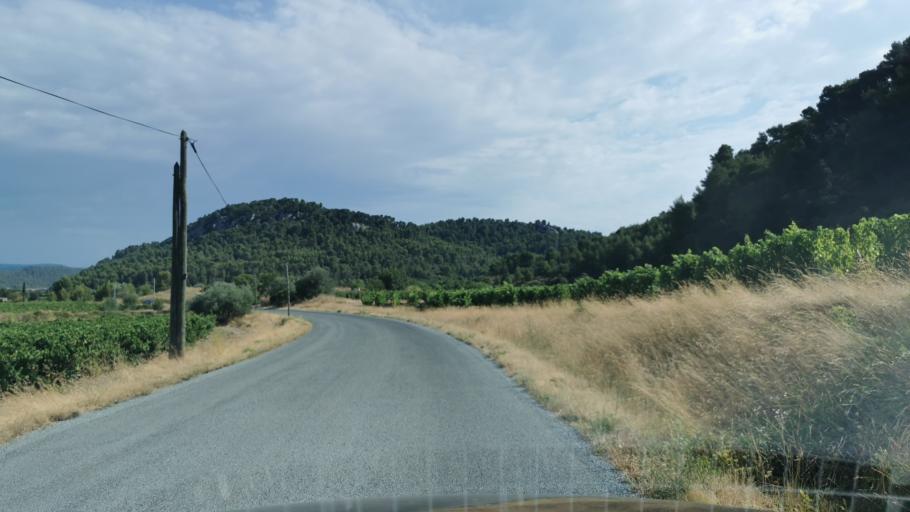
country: FR
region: Languedoc-Roussillon
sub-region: Departement de l'Aude
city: Bize-Minervois
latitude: 43.3213
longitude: 2.8812
